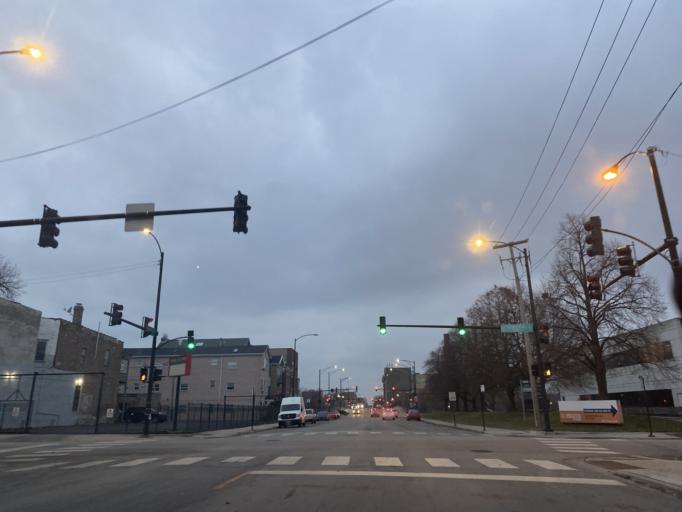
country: US
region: Illinois
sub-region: Cook County
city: Chicago
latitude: 41.8737
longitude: -87.6837
